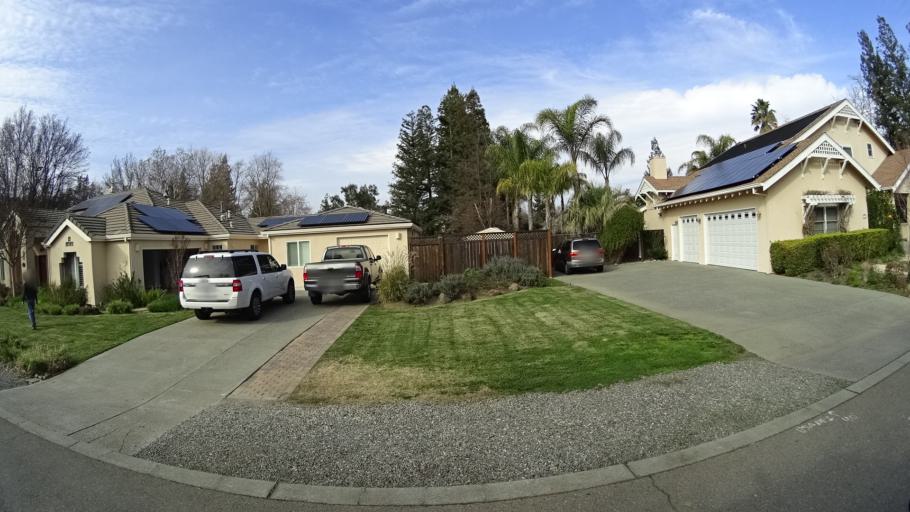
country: US
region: California
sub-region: Yolo County
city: Davis
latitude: 38.5378
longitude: -121.7157
